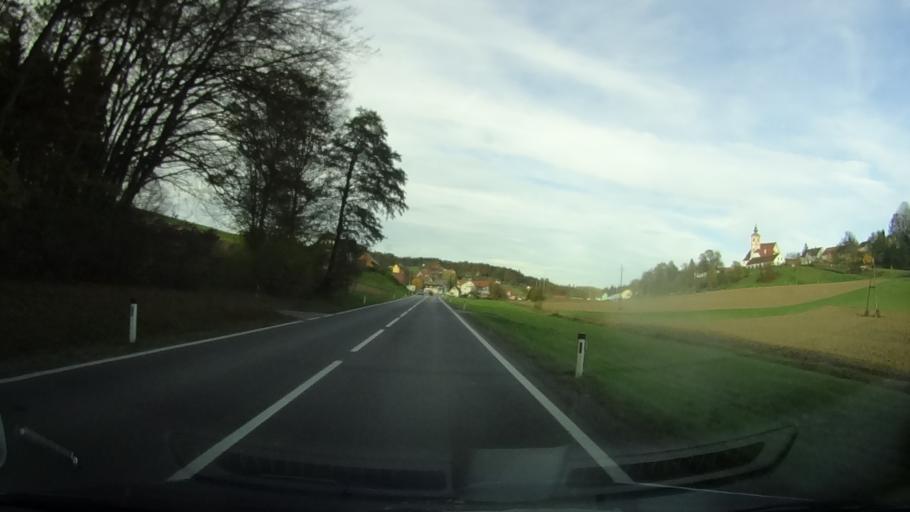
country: AT
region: Styria
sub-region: Politischer Bezirk Leibnitz
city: Pistorf
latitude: 46.7891
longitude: 15.3723
